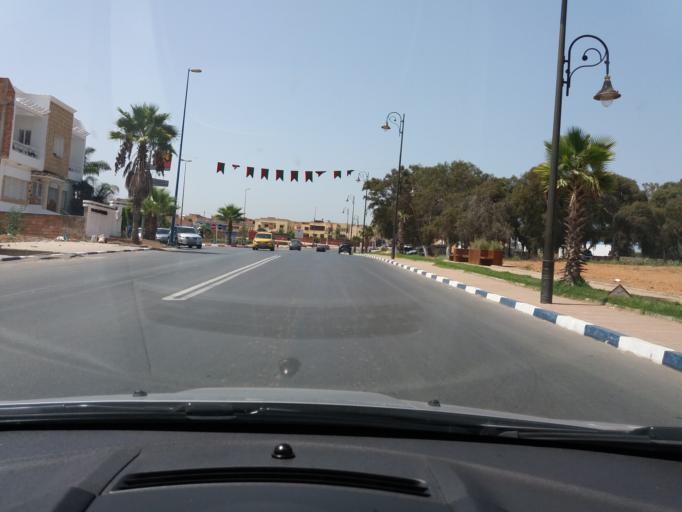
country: MA
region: Gharb-Chrarda-Beni Hssen
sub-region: Kenitra Province
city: Kenitra
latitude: 34.2679
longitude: -6.6433
